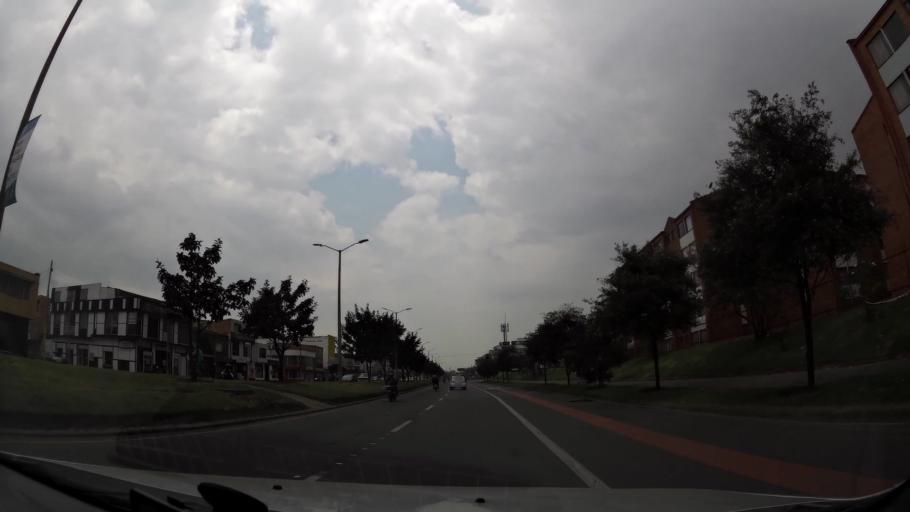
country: CO
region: Bogota D.C.
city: Bogota
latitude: 4.6006
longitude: -74.1181
